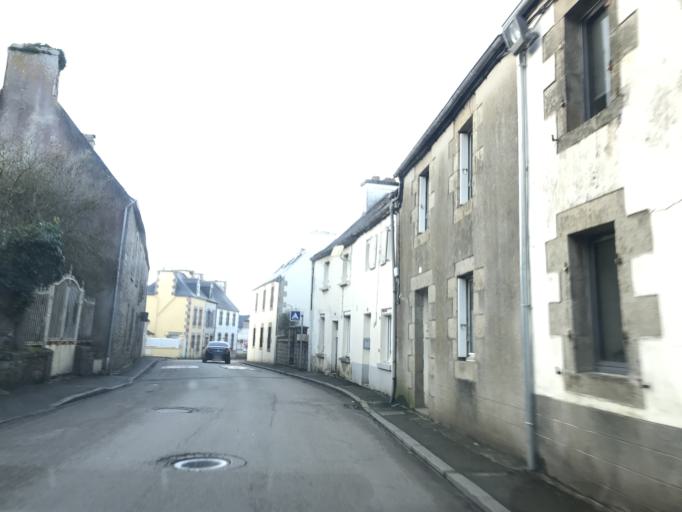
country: FR
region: Brittany
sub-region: Departement du Finistere
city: Lanmeur
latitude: 48.6464
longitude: -3.7141
